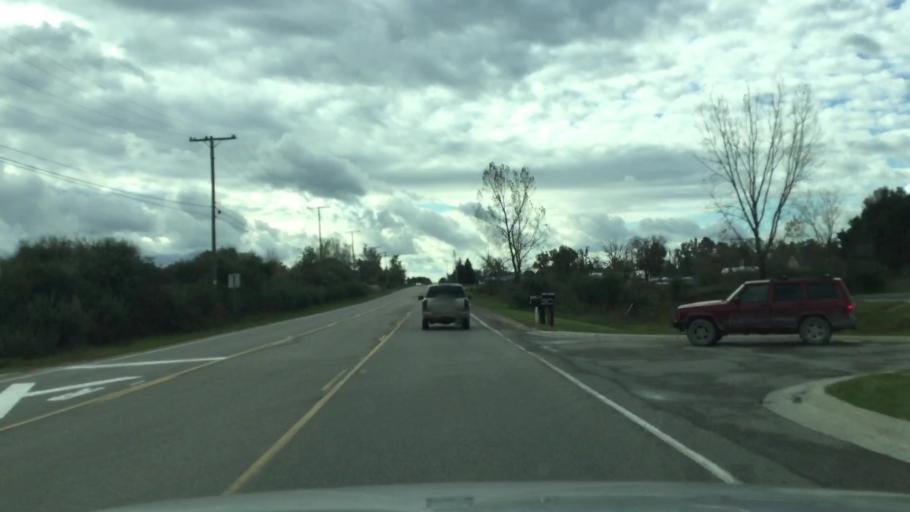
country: US
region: Michigan
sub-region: Lapeer County
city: Lapeer
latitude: 43.0396
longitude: -83.3619
